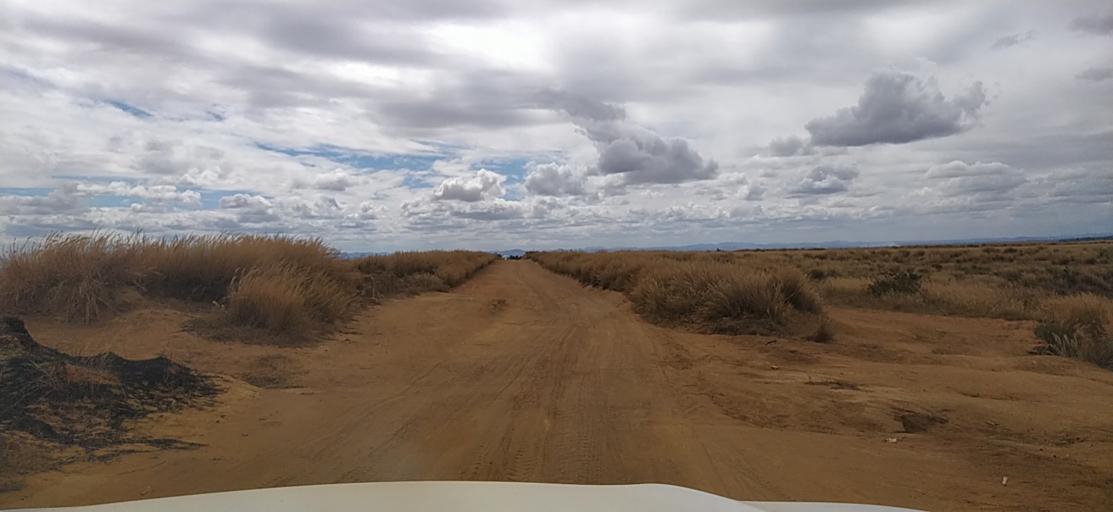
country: MG
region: Alaotra Mangoro
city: Ambatondrazaka
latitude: -17.9091
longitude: 48.2632
